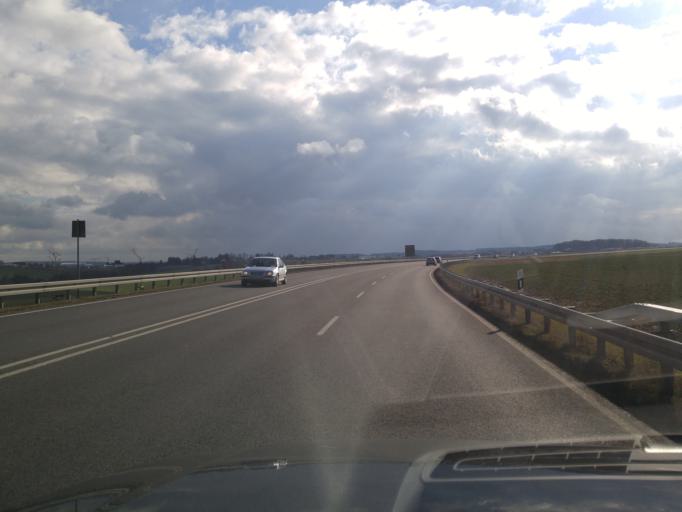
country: DE
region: Saxony
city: Lichtentanne
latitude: 50.6813
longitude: 12.4472
